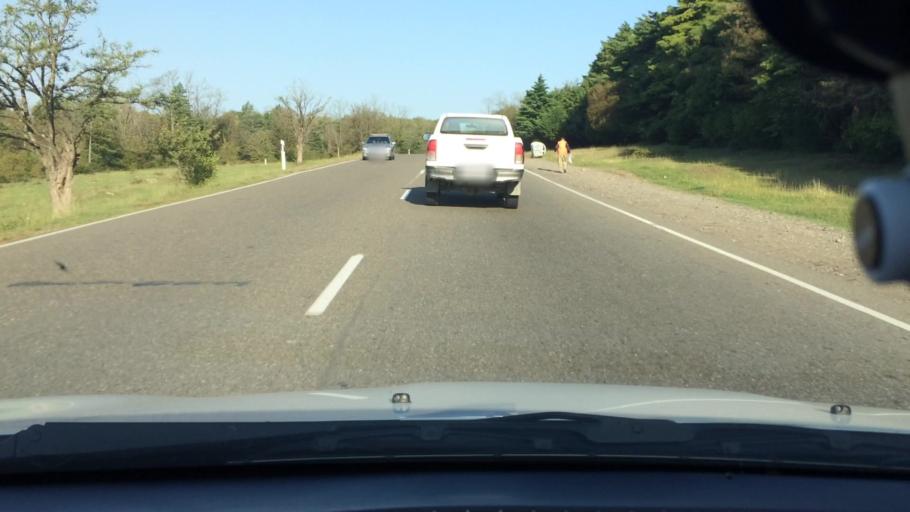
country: GE
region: Imereti
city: Kutaisi
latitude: 42.2307
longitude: 42.7777
